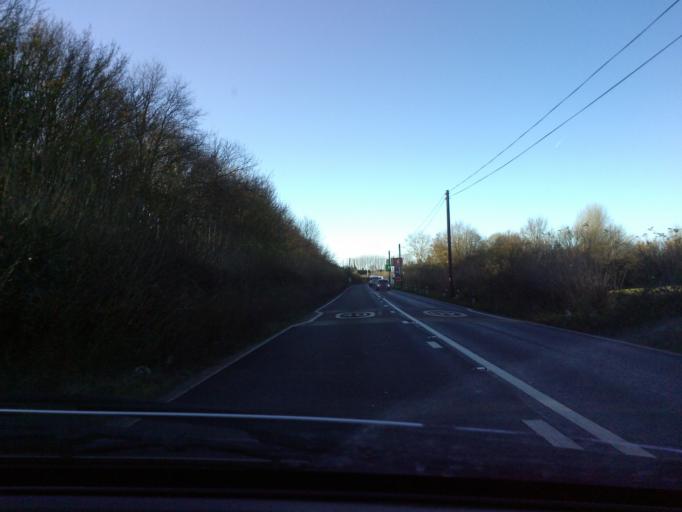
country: GB
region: England
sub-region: Dorset
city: Lytchett Matravers
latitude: 50.7750
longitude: -2.1503
